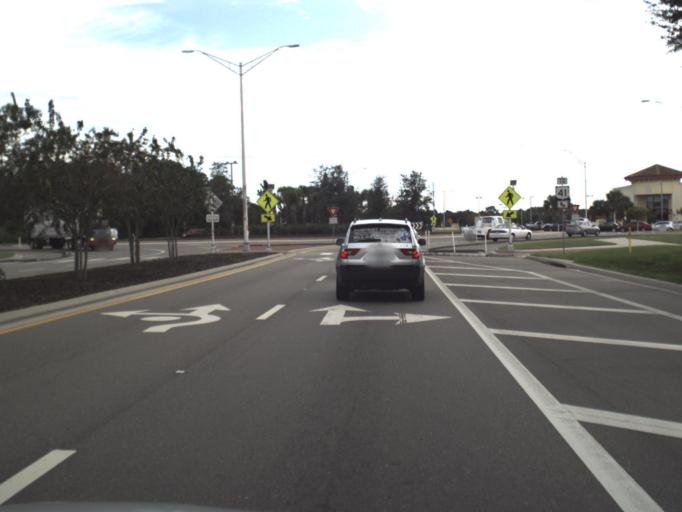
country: US
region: Florida
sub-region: Sarasota County
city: Plantation
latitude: 27.1006
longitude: -82.3845
